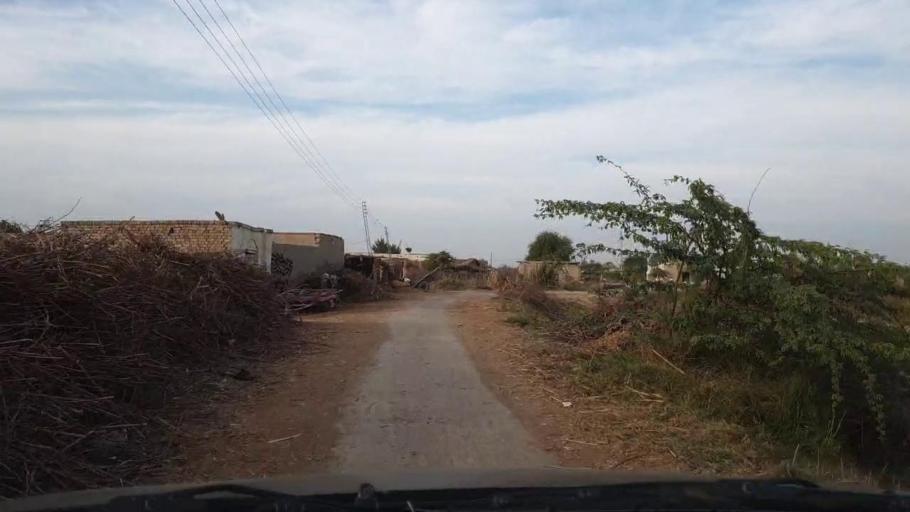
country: PK
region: Sindh
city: Khadro
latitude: 26.1674
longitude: 68.7262
